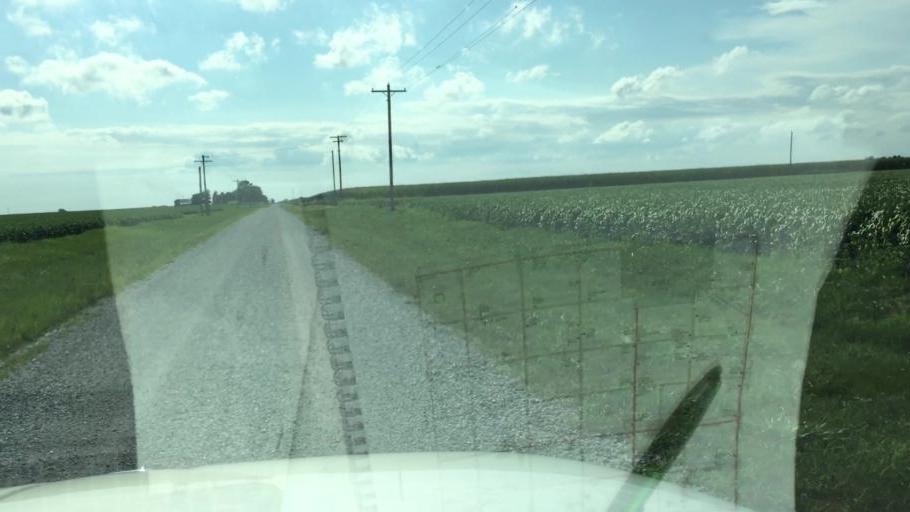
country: US
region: Illinois
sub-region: Hancock County
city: Nauvoo
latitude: 40.5214
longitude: -91.2822
